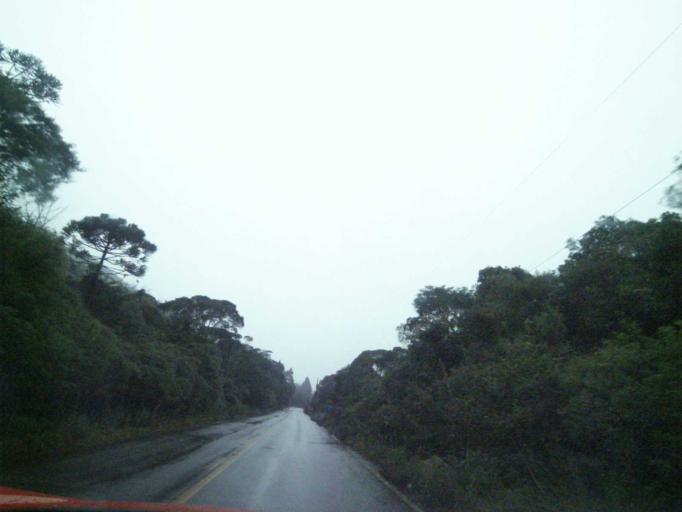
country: BR
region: Santa Catarina
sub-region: Anitapolis
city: Anitapolis
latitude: -27.7785
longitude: -49.0420
